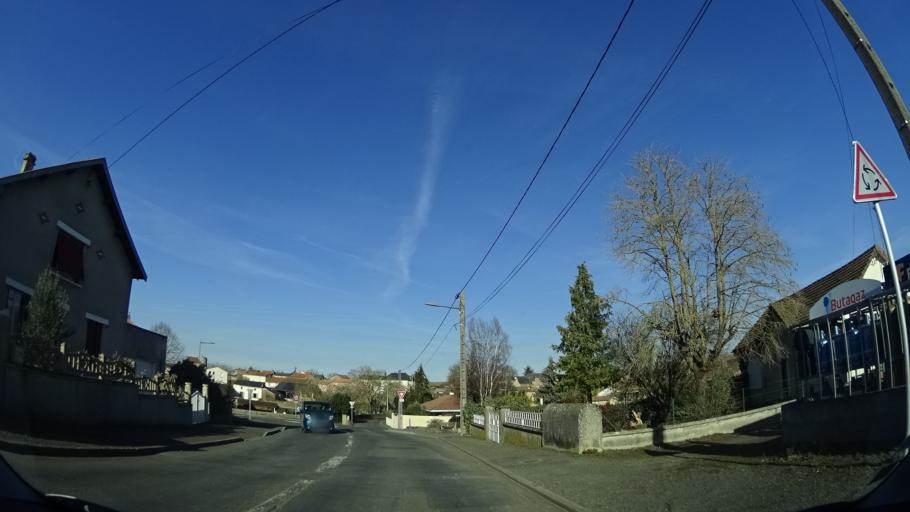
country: FR
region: Poitou-Charentes
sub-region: Departement des Deux-Sevres
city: Airvault
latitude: 46.8268
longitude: -0.1328
